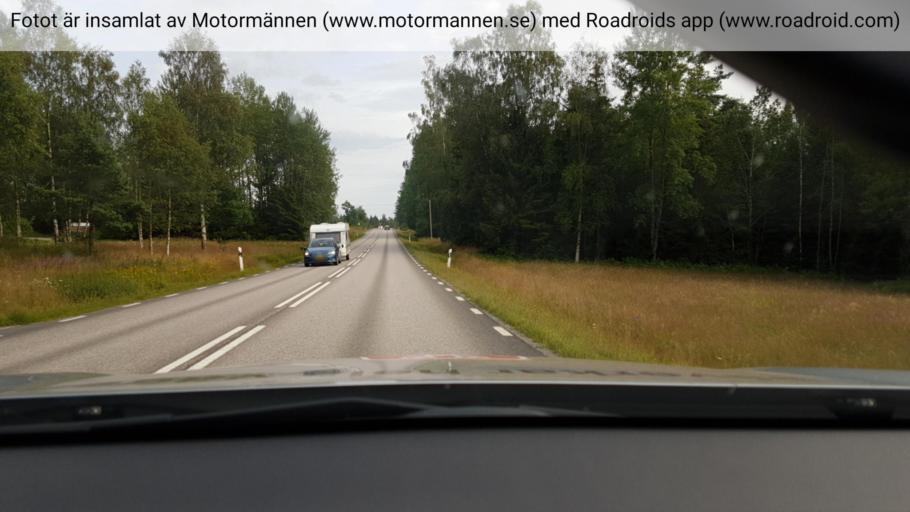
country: SE
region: Vaestra Goetaland
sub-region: Uddevalla Kommun
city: Uddevalla
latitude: 58.4355
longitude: 12.0179
